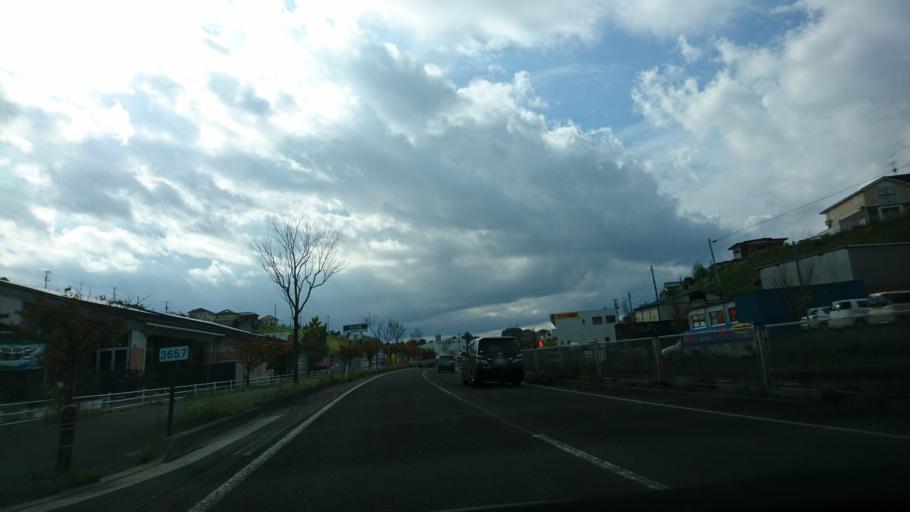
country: JP
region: Miyagi
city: Tomiya
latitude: 38.3693
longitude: 140.8742
